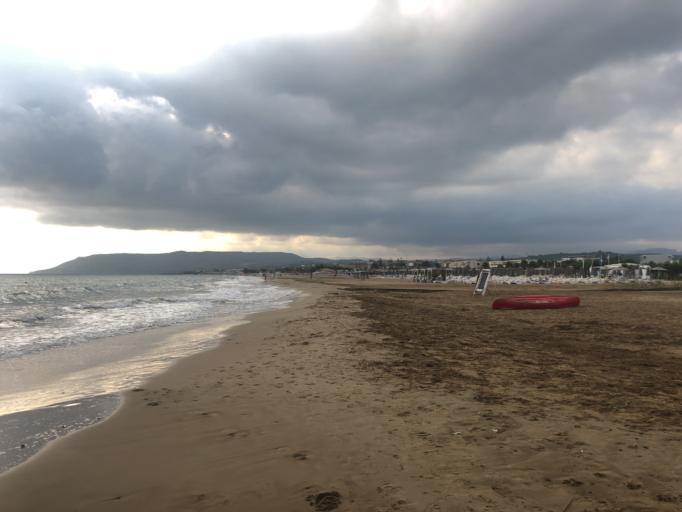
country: GR
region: Crete
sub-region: Nomos Chanias
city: Georgioupolis
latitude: 35.3552
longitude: 24.2897
